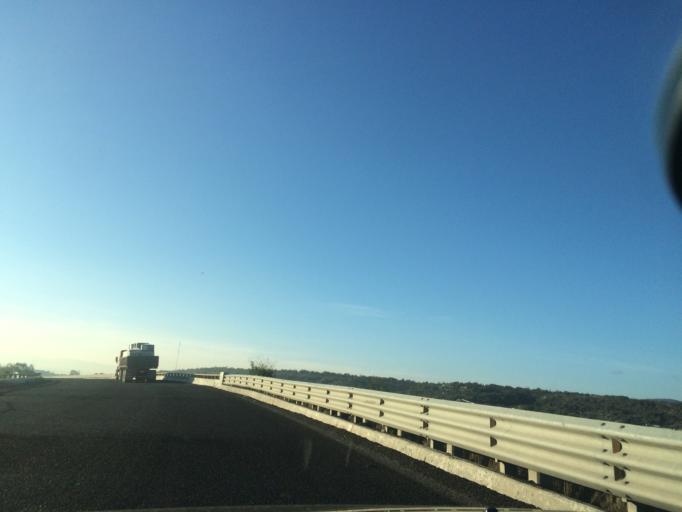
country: MX
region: Puebla
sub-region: Santiago Miahuatlan
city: San Jose Monte Chiquito
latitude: 18.4862
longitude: -97.4570
